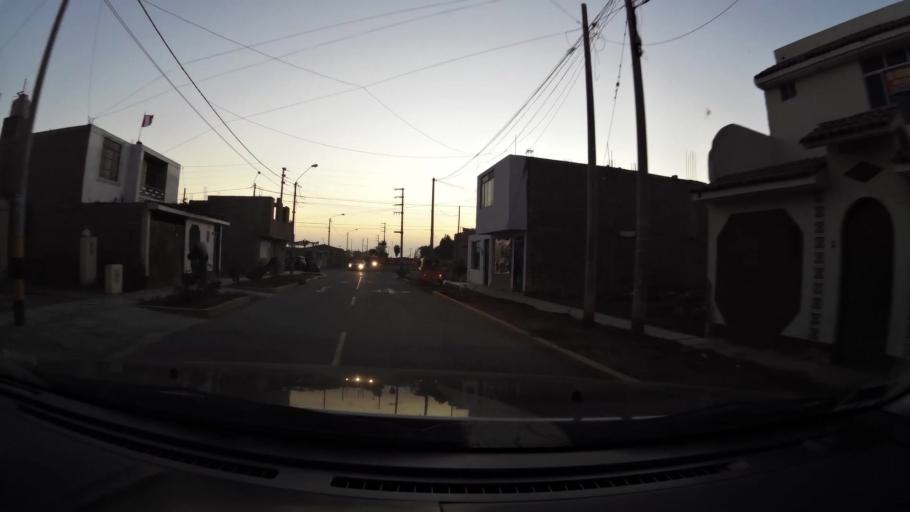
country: PE
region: Ica
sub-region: Provincia de Pisco
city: Pisco
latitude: -13.7069
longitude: -76.2077
